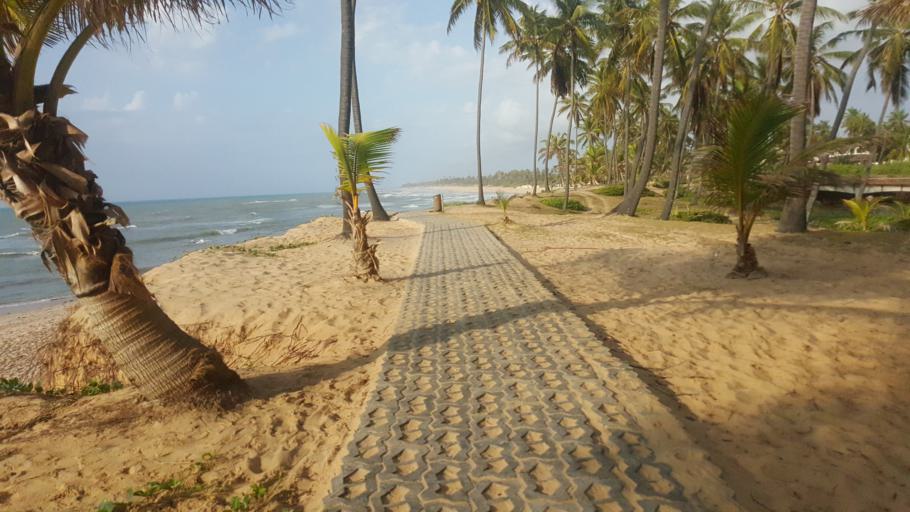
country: BR
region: Bahia
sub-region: Mata De Sao Joao
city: Mata de Sao Joao
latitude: -12.4416
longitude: -37.9196
